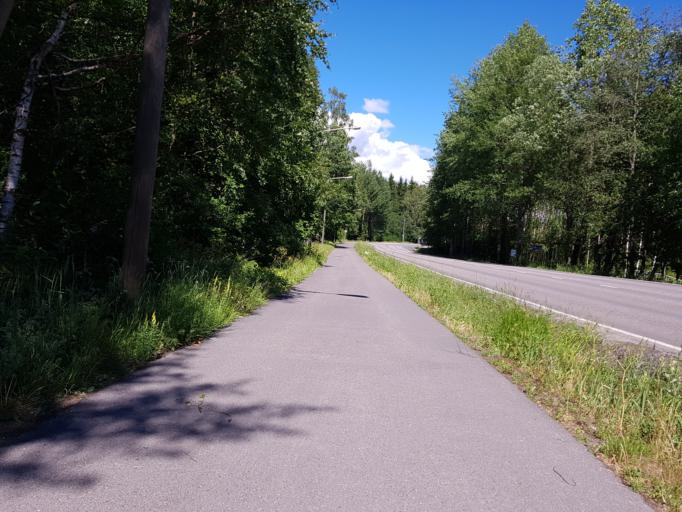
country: FI
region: Uusimaa
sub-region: Helsinki
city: Teekkarikylae
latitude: 60.3045
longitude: 24.8616
